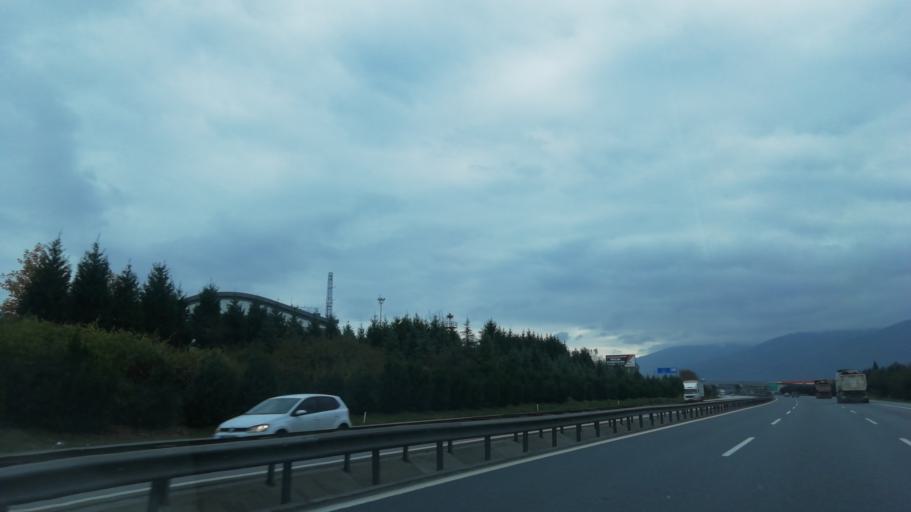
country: TR
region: Kocaeli
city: Kosekoy
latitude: 40.7358
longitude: 30.0506
